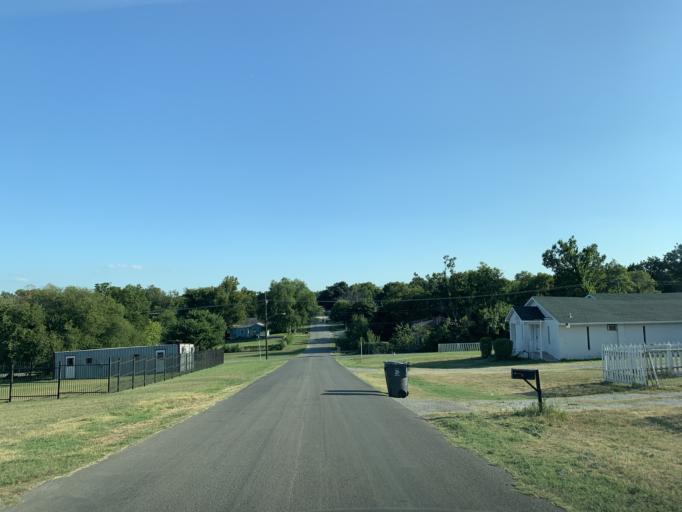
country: US
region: Texas
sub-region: Dallas County
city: Hutchins
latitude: 32.6703
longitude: -96.7780
